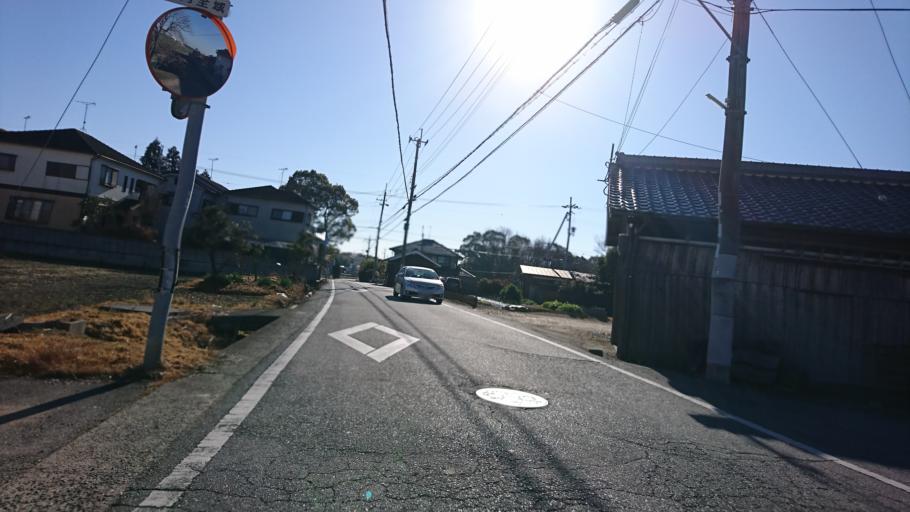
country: JP
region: Hyogo
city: Miki
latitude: 34.7435
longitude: 134.9399
